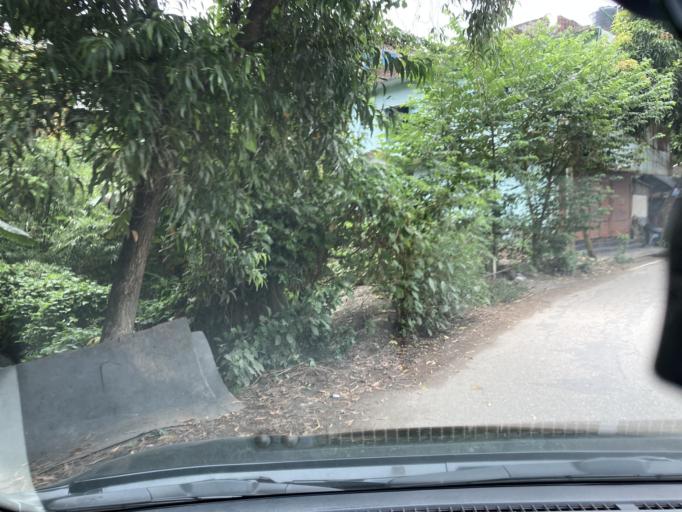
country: BD
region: Dhaka
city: Dohar
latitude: 23.7604
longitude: 90.2052
